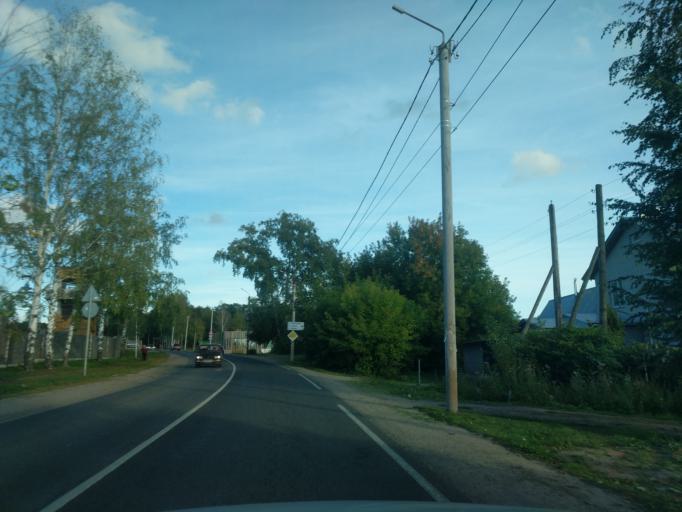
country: RU
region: Kirov
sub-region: Kirovo-Chepetskiy Rayon
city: Kirov
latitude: 58.6120
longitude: 49.7817
